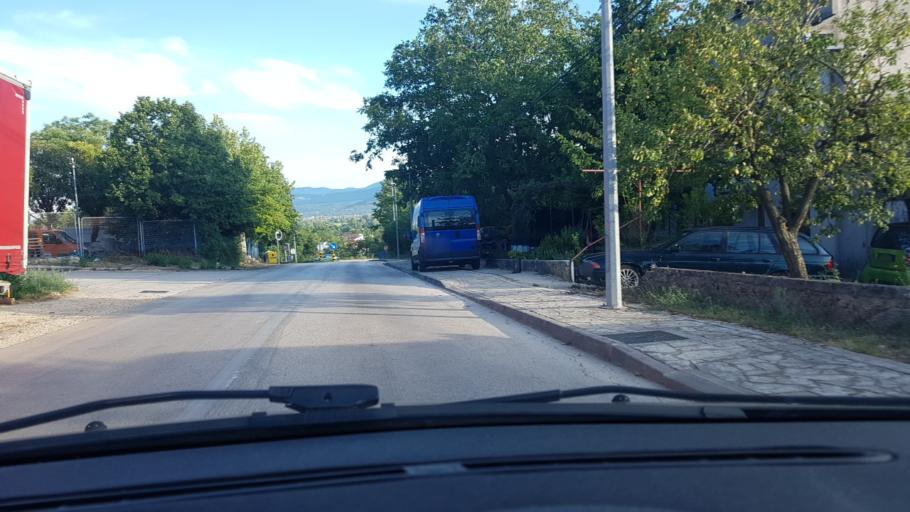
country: HR
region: Splitsko-Dalmatinska
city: Imotski
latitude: 43.4435
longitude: 17.2063
